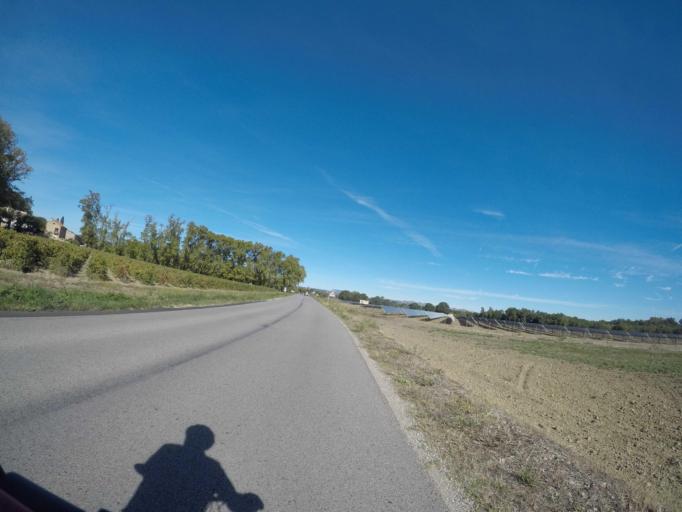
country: FR
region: Languedoc-Roussillon
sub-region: Departement des Pyrenees-Orientales
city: Le Soler
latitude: 42.6635
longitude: 2.7946
